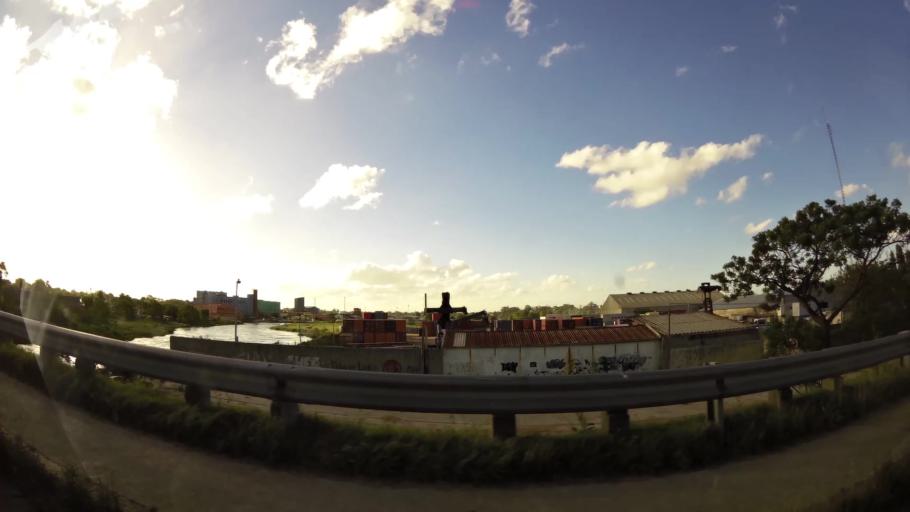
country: UY
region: Montevideo
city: Montevideo
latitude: -34.8725
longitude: -56.2435
